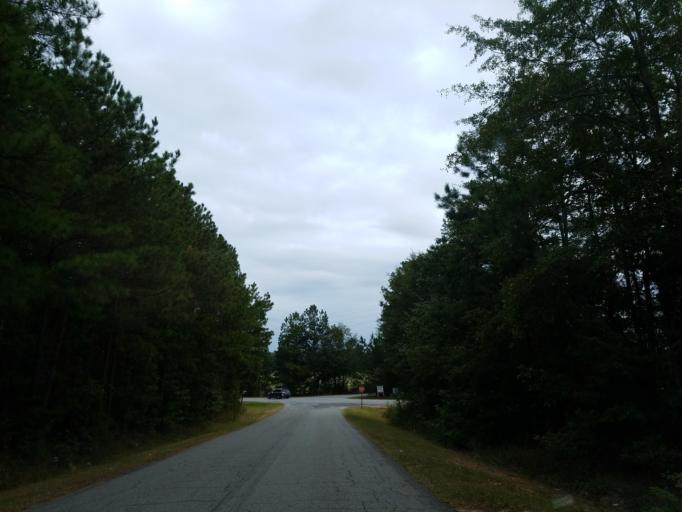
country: US
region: Georgia
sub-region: Lamar County
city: Barnesville
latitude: 33.1602
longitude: -84.0736
